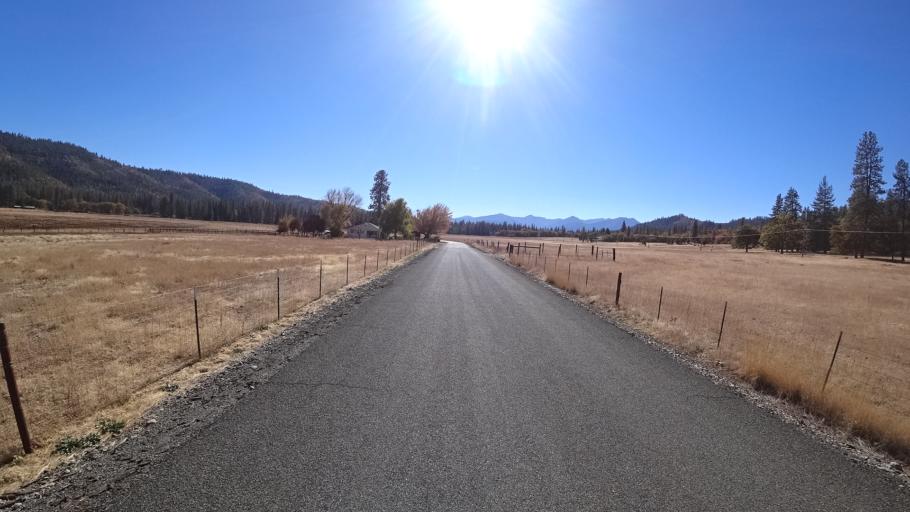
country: US
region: California
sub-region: Siskiyou County
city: Yreka
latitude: 41.5935
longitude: -122.9117
